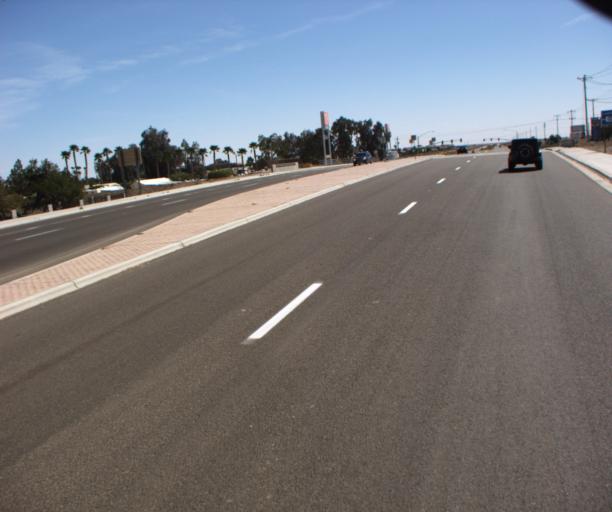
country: US
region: Arizona
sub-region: Yuma County
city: Fortuna Foothills
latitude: 32.6727
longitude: -114.5215
